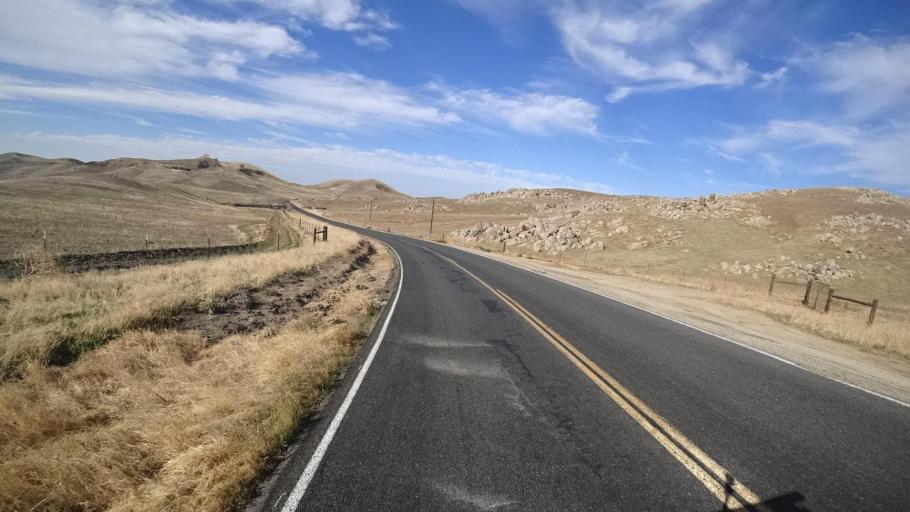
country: US
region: California
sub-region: Kern County
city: Oildale
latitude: 35.6130
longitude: -118.8689
